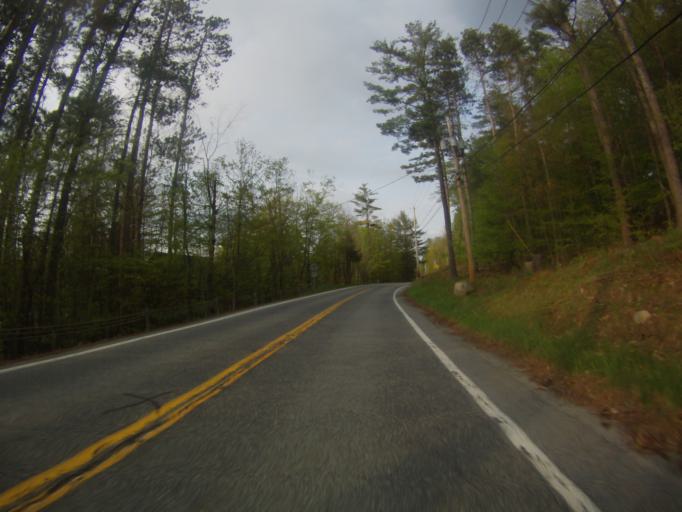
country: US
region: New York
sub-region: Warren County
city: Warrensburg
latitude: 43.7173
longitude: -73.6959
